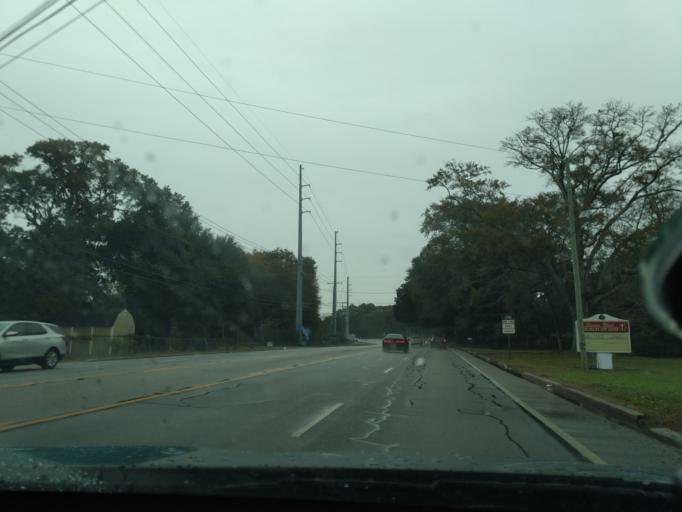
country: US
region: South Carolina
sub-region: Charleston County
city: Folly Beach
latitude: 32.7063
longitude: -79.9646
